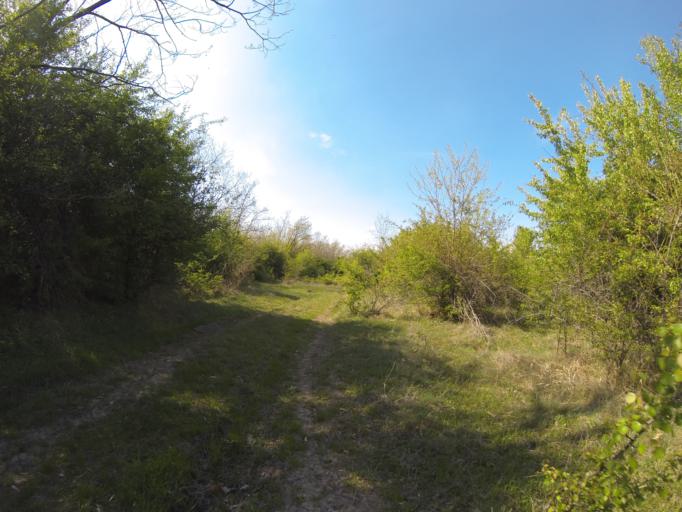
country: RO
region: Gorj
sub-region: Comuna Crusetu
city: Crusetu
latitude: 44.6298
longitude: 23.6373
